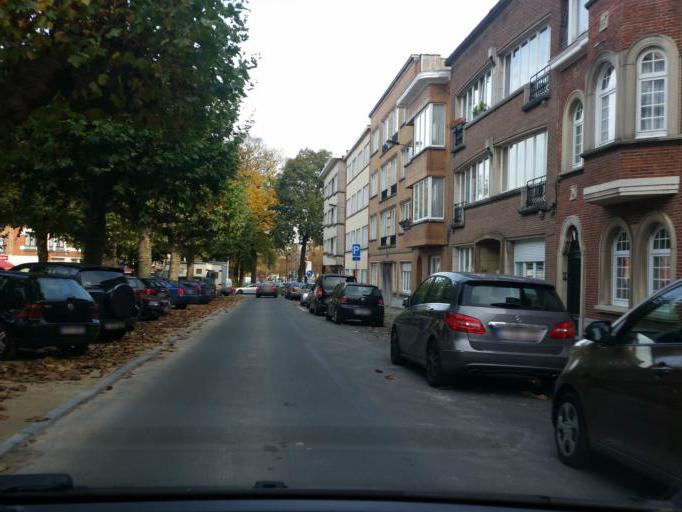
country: BE
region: Brussels Capital
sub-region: Bruxelles-Capitale
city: Brussels
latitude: 50.8692
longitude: 4.3207
